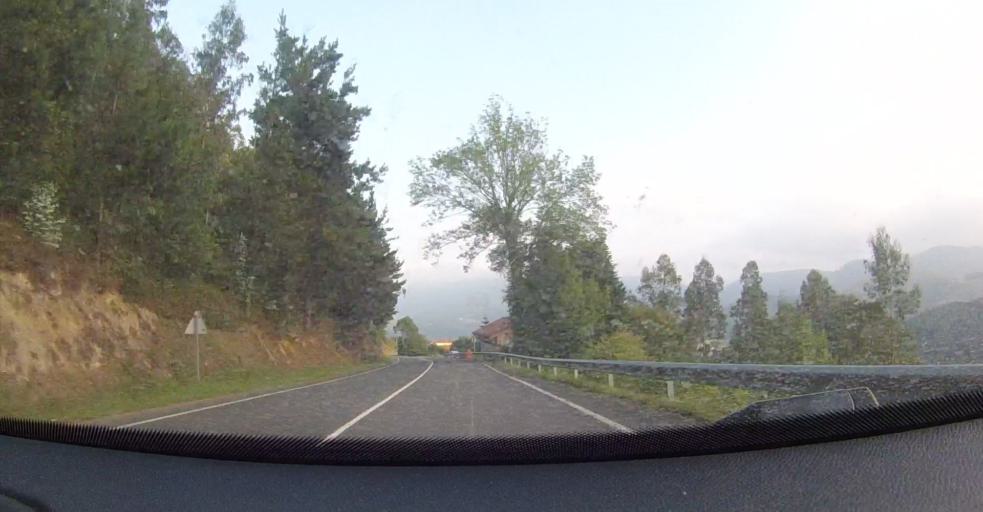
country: ES
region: Basque Country
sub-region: Bizkaia
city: Sopuerta
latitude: 43.2944
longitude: -3.1652
